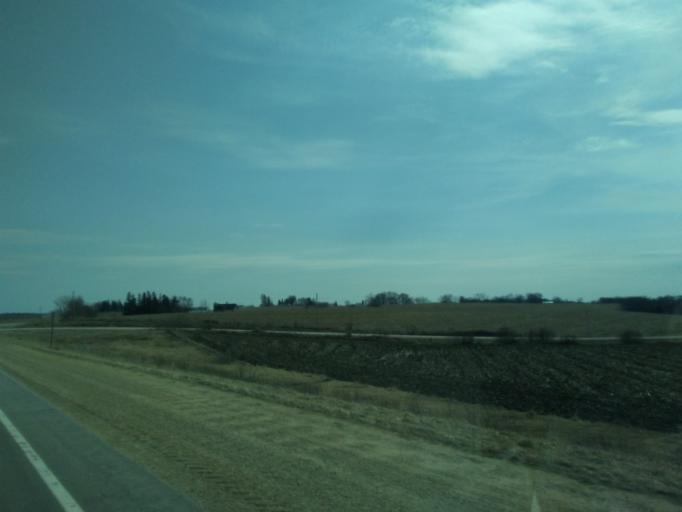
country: US
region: Iowa
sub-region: Winneshiek County
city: Decorah
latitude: 43.4519
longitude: -91.8662
